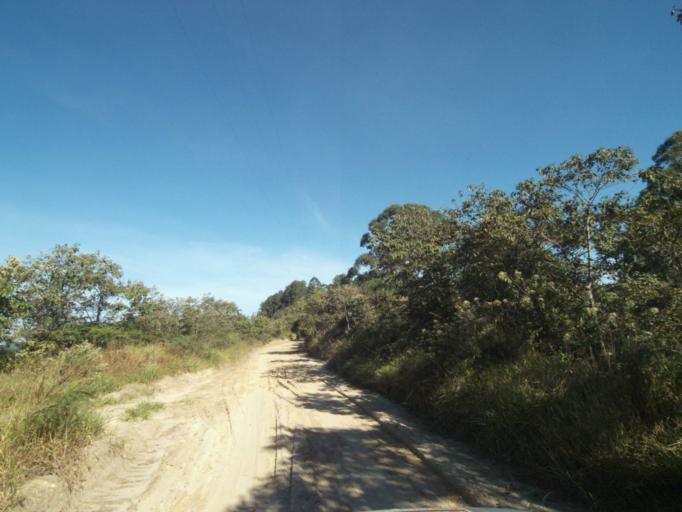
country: BR
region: Parana
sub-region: Tibagi
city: Tibagi
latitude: -24.5680
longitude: -50.4711
